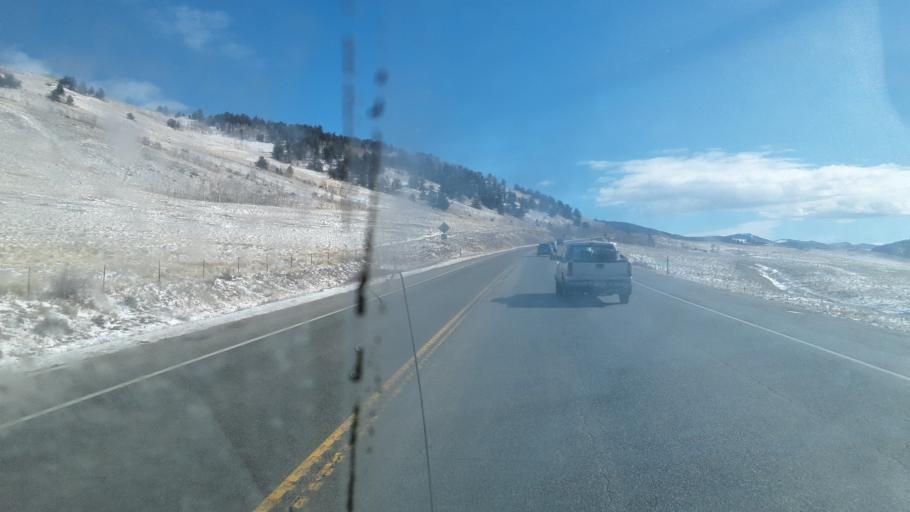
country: US
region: Colorado
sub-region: Summit County
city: Breckenridge
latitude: 39.4055
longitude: -105.7707
